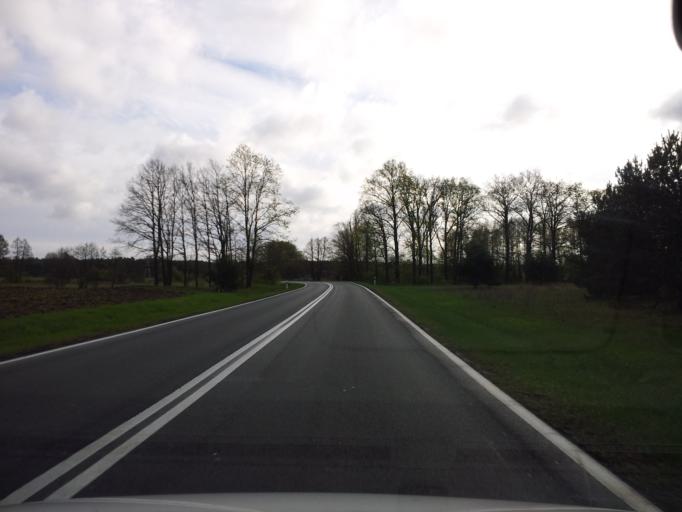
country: PL
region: Lubusz
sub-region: Powiat zielonogorski
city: Swidnica
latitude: 51.8747
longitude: 15.3701
